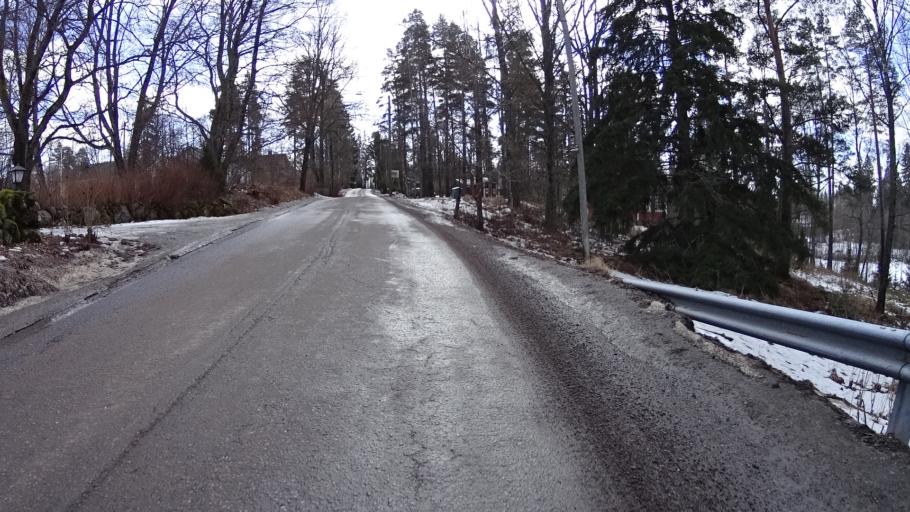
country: FI
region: Uusimaa
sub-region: Helsinki
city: Kauniainen
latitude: 60.2665
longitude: 24.6900
